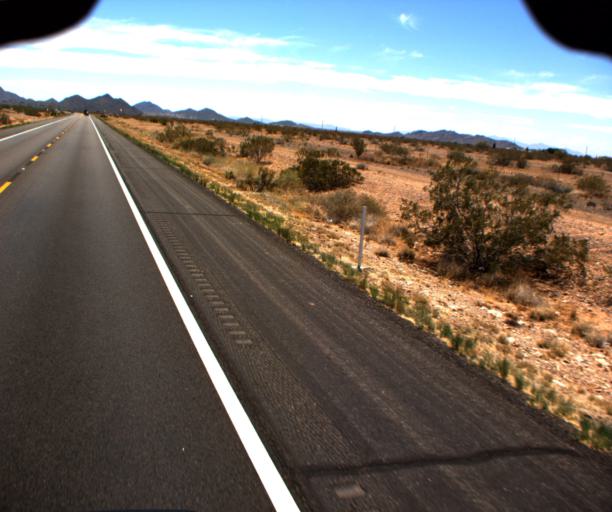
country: US
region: Arizona
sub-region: Maricopa County
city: Anthem
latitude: 33.8104
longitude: -112.2467
